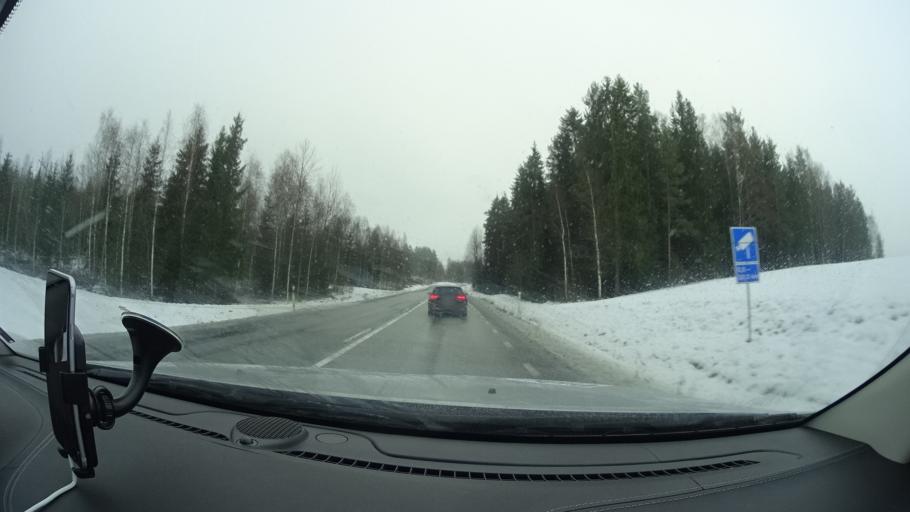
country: SE
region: OErebro
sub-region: Lindesbergs Kommun
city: Stora
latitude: 59.8060
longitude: 15.1477
